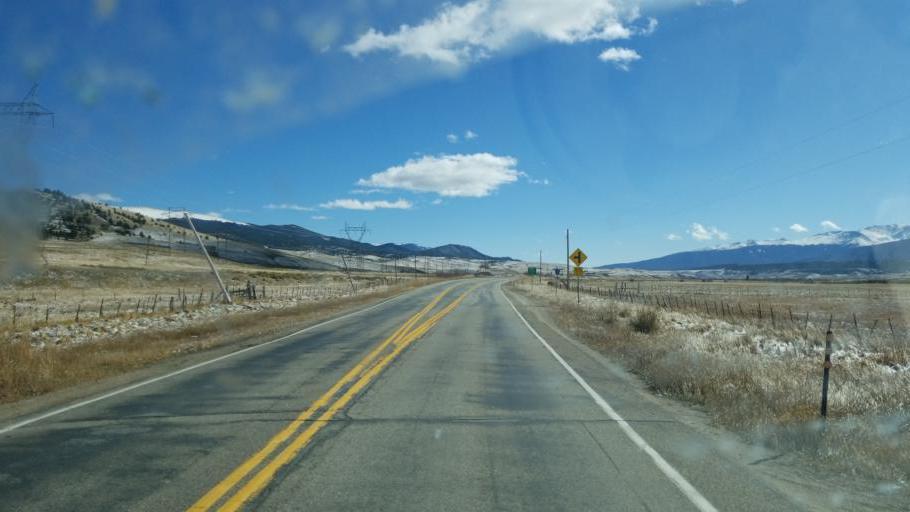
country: US
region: Colorado
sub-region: Lake County
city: Leadville
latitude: 39.1786
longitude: -106.3235
